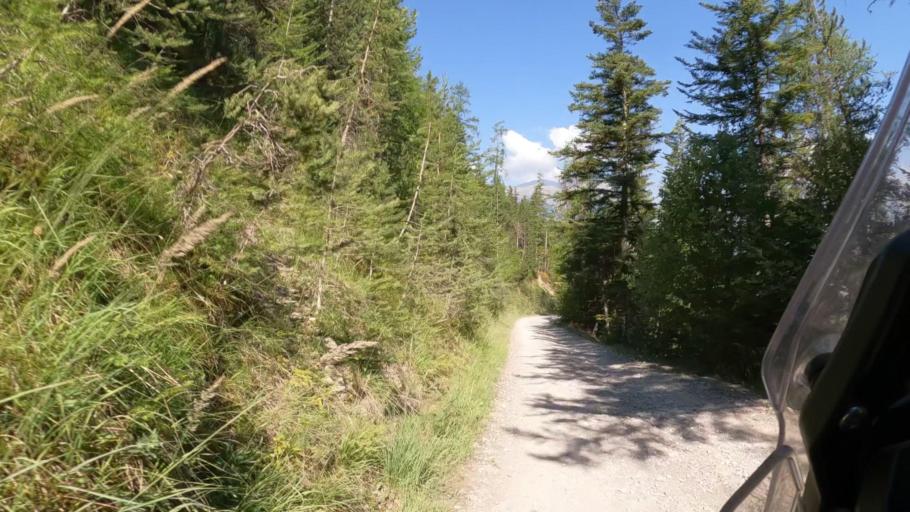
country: FR
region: Provence-Alpes-Cote d'Azur
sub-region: Departement des Hautes-Alpes
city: Embrun
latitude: 44.5878
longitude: 6.5593
